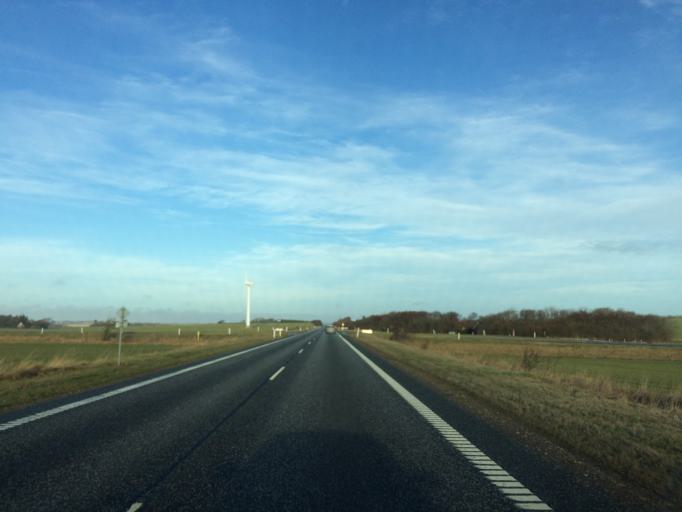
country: DK
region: North Denmark
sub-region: Thisted Kommune
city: Hurup
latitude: 56.7682
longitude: 8.4585
